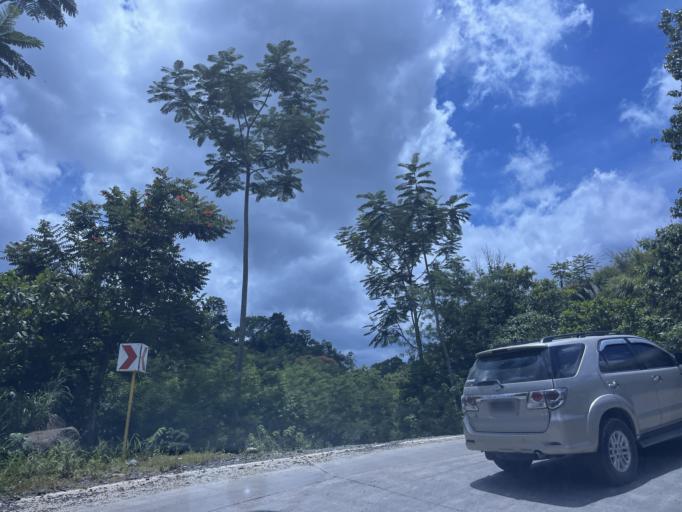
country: PH
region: Northern Mindanao
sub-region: Province of Bukidnon
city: Kisolon
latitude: 8.3083
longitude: 124.9637
